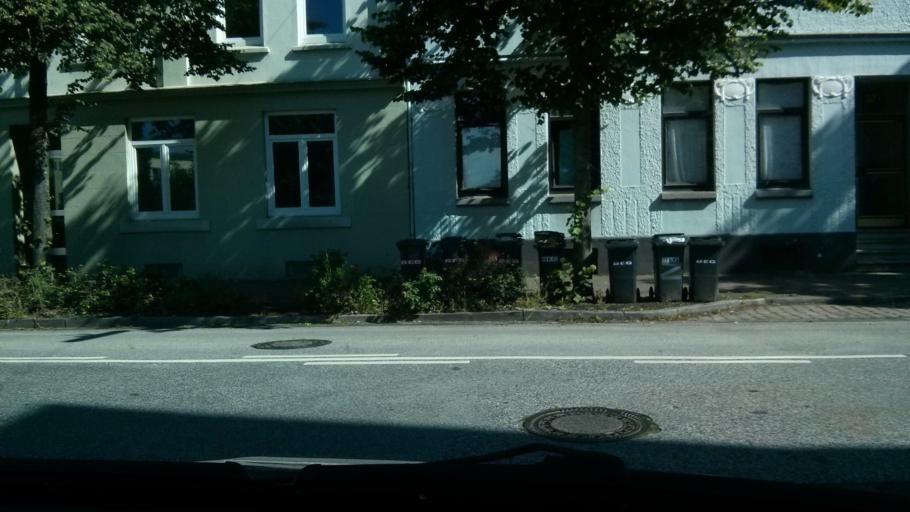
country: DE
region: Bremen
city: Bremerhaven
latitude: 53.5268
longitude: 8.5940
